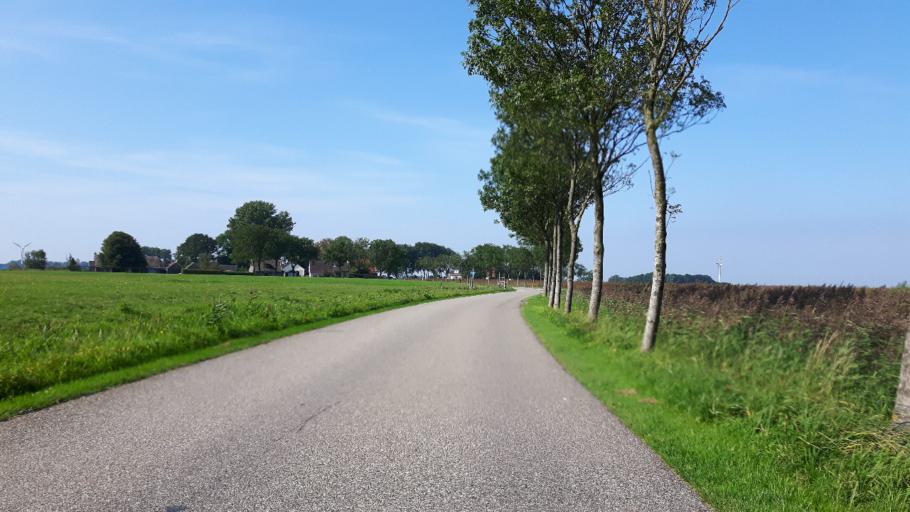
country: NL
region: Friesland
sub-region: Gemeente Ferwerderadiel
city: Ferwert
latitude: 53.3517
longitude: 5.8568
